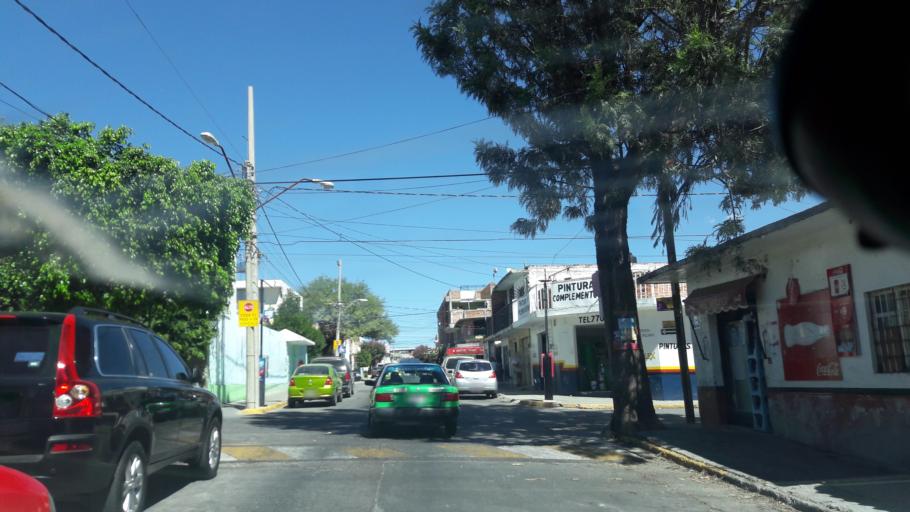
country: MX
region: Guanajuato
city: Leon
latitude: 21.1100
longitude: -101.6969
